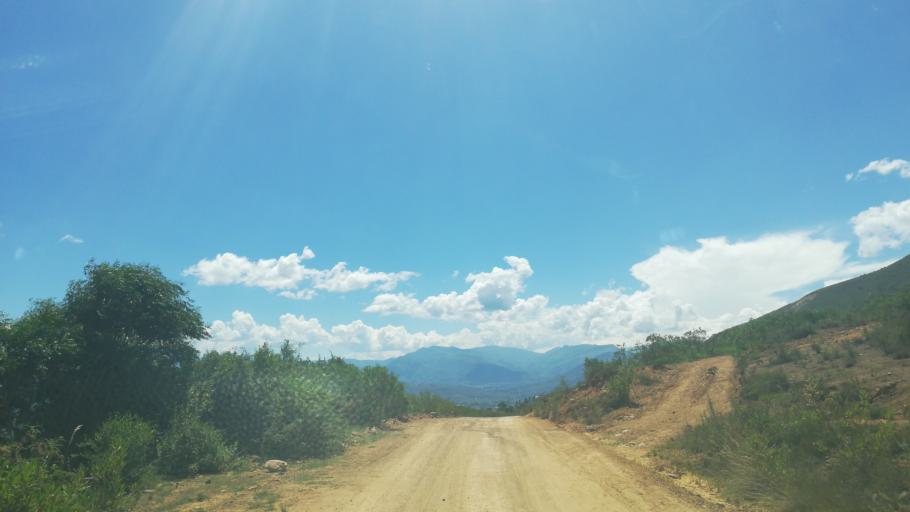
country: BO
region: Cochabamba
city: Totora
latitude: -17.7347
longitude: -65.2263
